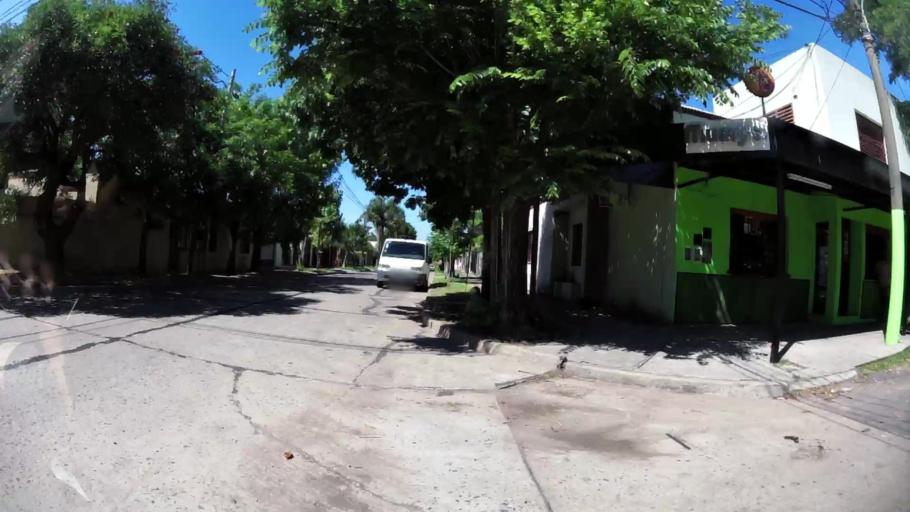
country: AR
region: Buenos Aires
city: Ituzaingo
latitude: -34.6601
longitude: -58.6447
